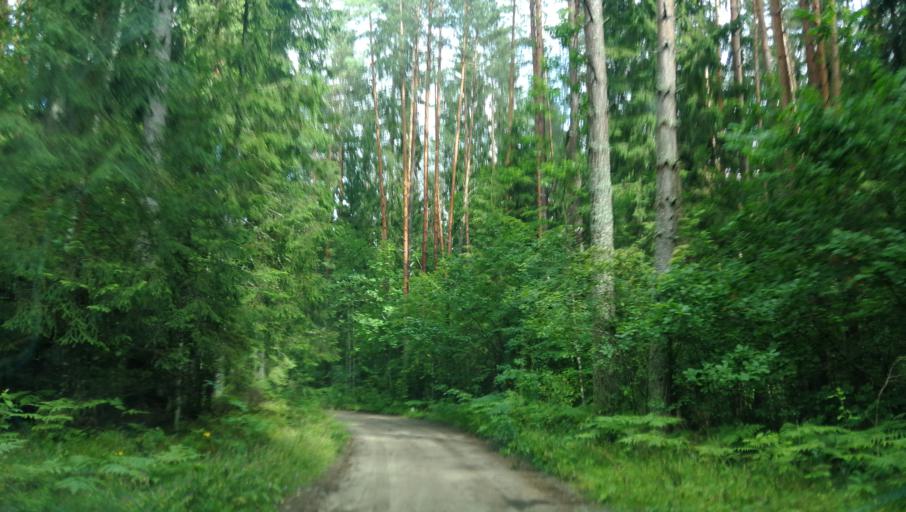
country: LV
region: Cesu Rajons
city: Cesis
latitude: 57.3094
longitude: 25.2163
